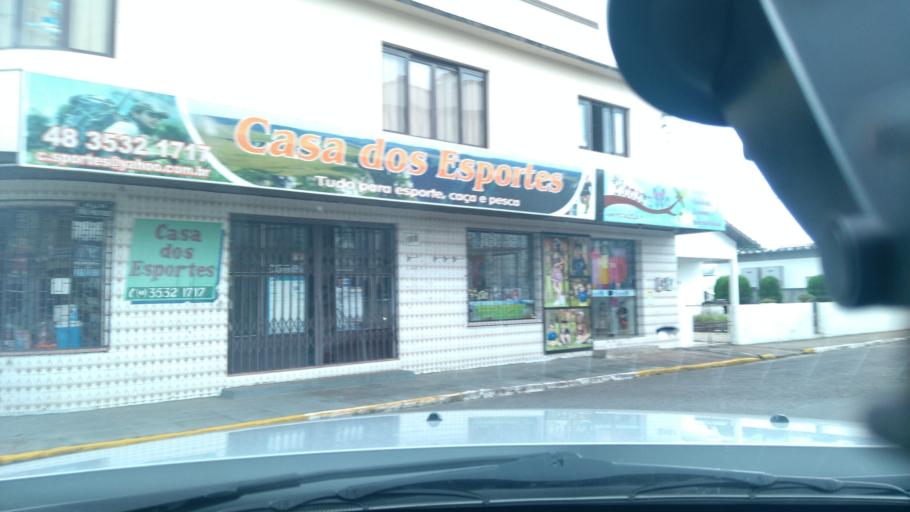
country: BR
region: Rio Grande do Sul
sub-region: Torres
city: Torres
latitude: -29.1967
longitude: -49.9510
